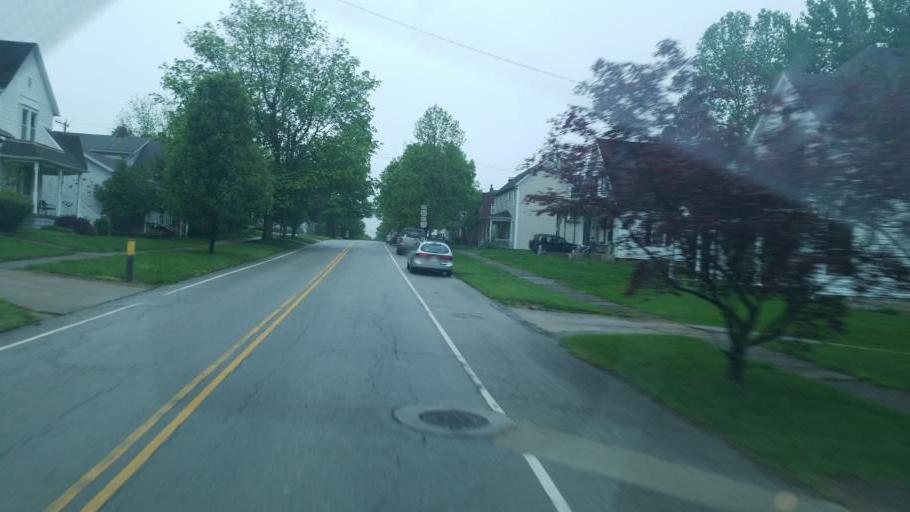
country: US
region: Ohio
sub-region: Highland County
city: Hillsboro
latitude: 39.1998
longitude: -83.6140
